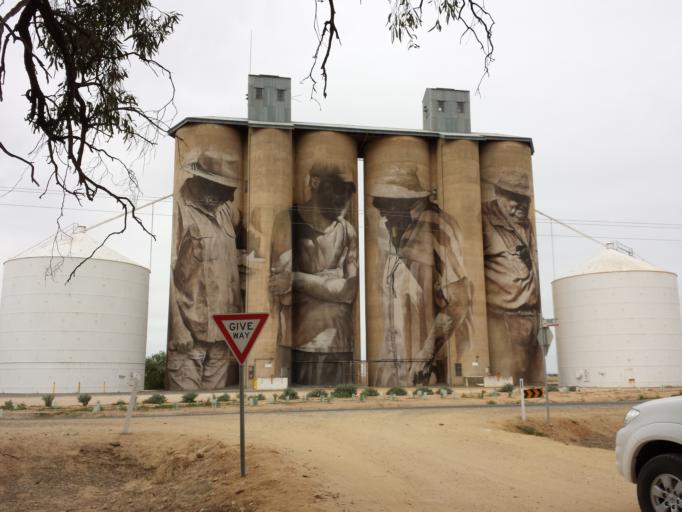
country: AU
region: Victoria
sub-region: Horsham
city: Horsham
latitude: -36.0784
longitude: 142.4209
